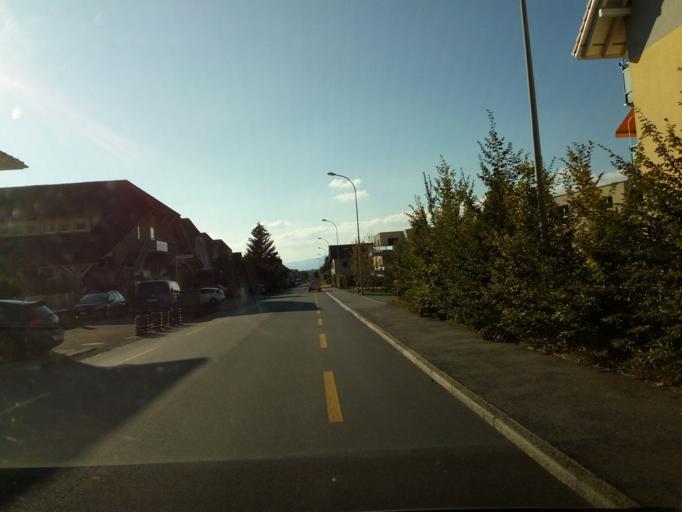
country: CH
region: Bern
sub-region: Seeland District
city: Schupfen
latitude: 47.0435
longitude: 7.3791
